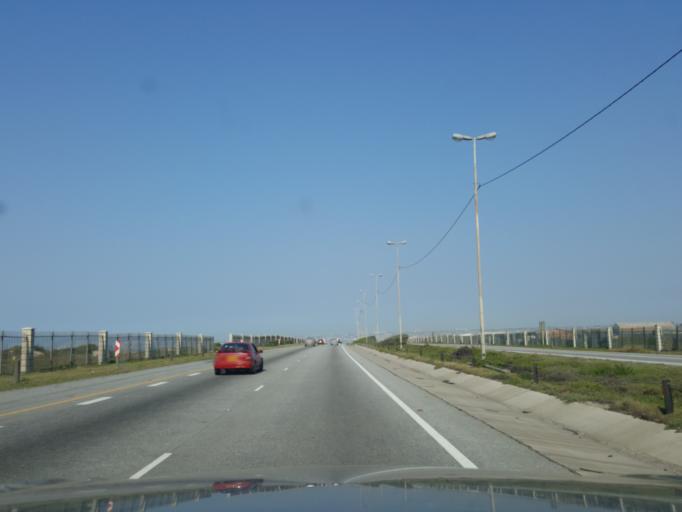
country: ZA
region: Eastern Cape
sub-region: Nelson Mandela Bay Metropolitan Municipality
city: Port Elizabeth
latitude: -33.8870
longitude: 25.6229
